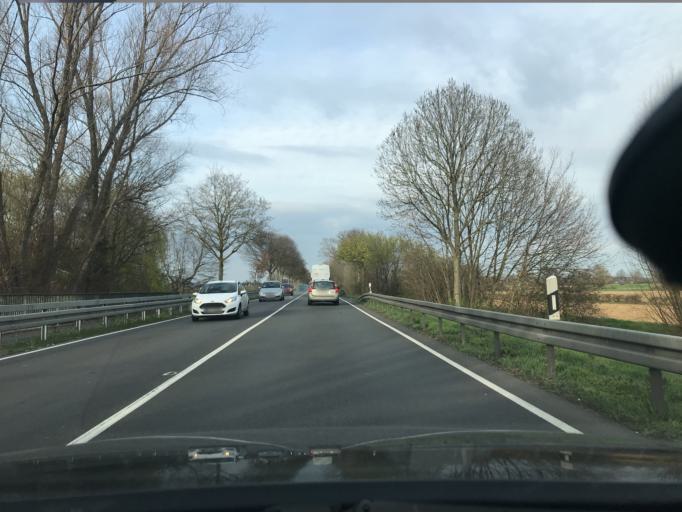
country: DE
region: North Rhine-Westphalia
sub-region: Regierungsbezirk Dusseldorf
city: Alpen
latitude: 51.5989
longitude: 6.5424
